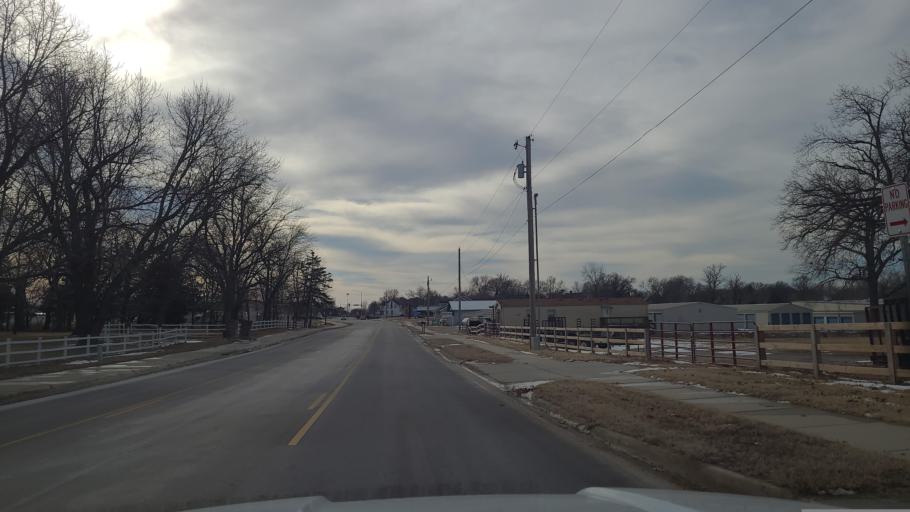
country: US
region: Kansas
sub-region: Douglas County
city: Baldwin City
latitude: 38.7847
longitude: -95.1864
